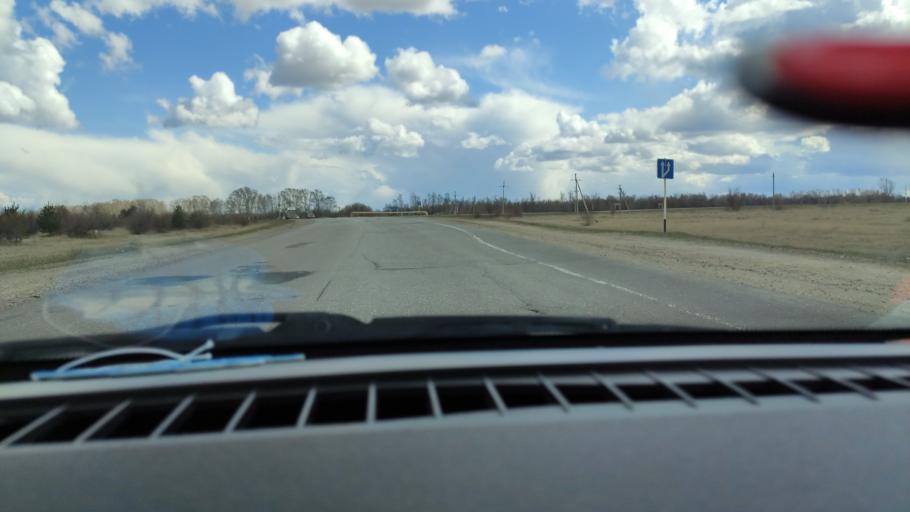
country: RU
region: Samara
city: Varlamovo
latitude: 53.1234
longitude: 48.2982
